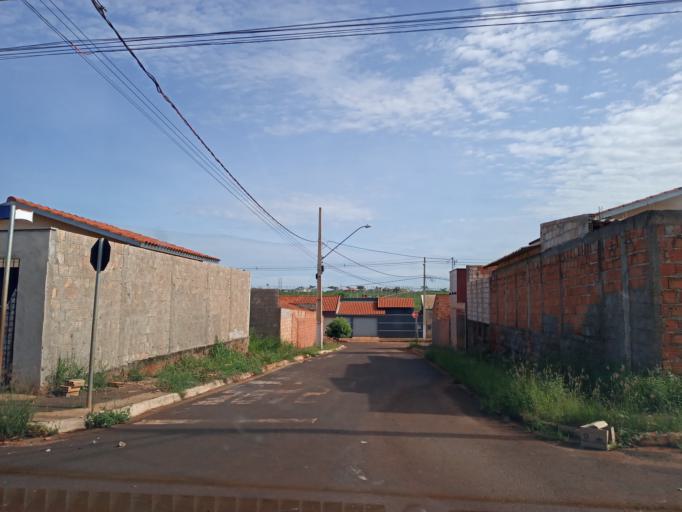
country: BR
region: Goias
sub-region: Itumbiara
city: Itumbiara
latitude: -18.4358
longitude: -49.1814
